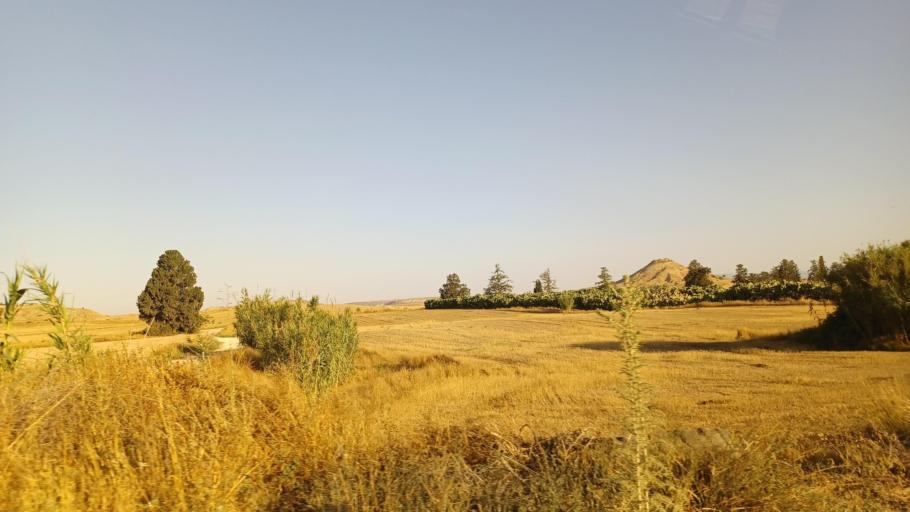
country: CY
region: Larnaka
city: Athienou
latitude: 35.0511
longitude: 33.4996
